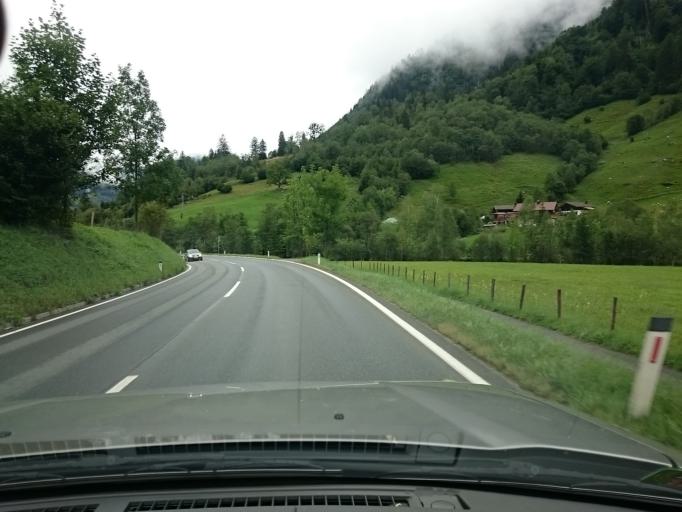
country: AT
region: Salzburg
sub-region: Politischer Bezirk Zell am See
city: Bruck an der Grossglocknerstrasse
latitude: 47.2596
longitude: 12.8253
